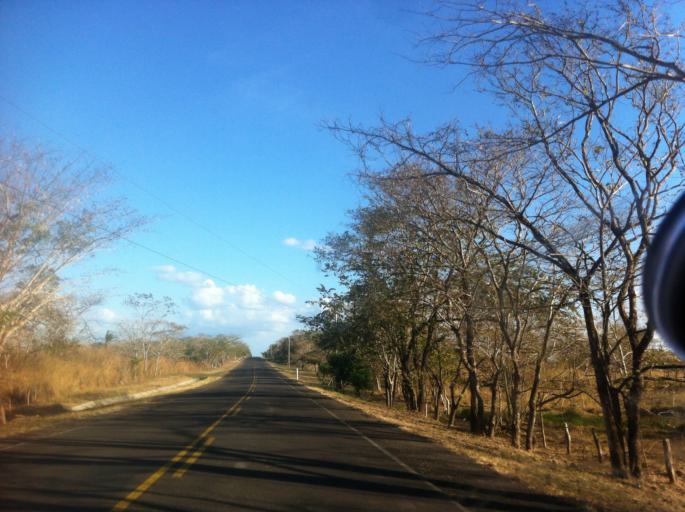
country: NI
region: Rio San Juan
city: Morrito
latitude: 11.7457
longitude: -84.9907
